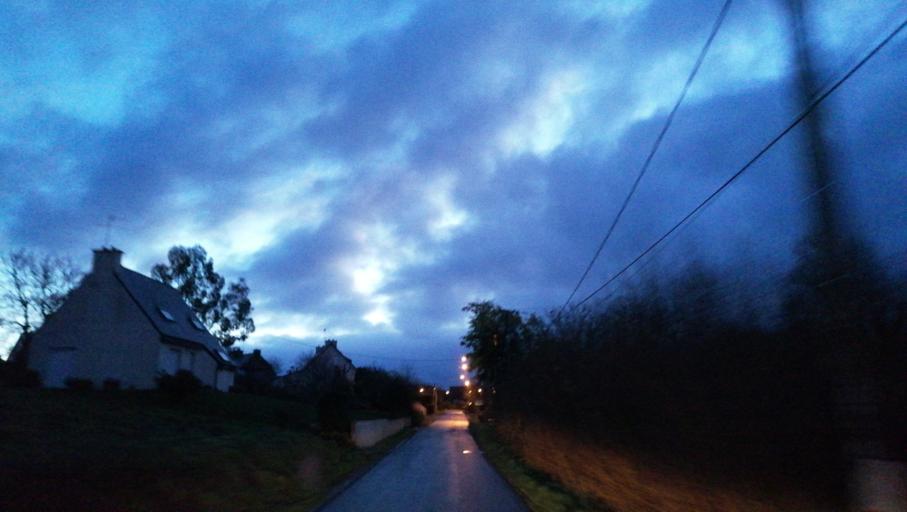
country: FR
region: Brittany
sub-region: Departement des Cotes-d'Armor
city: Plelo
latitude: 48.5567
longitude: -2.9532
